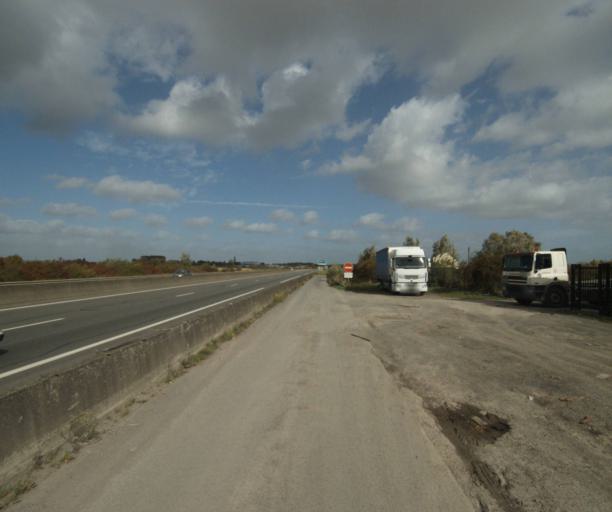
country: FR
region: Nord-Pas-de-Calais
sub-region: Departement du Nord
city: Illies
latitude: 50.5504
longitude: 2.8268
